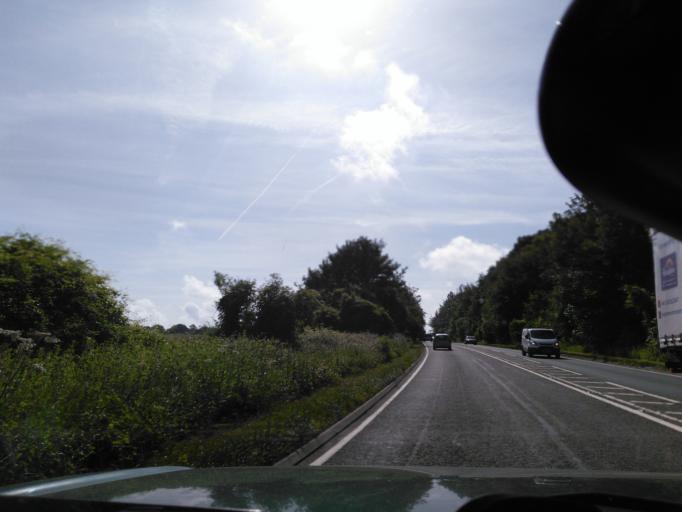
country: GB
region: England
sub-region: Wiltshire
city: Alderbury
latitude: 51.0232
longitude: -1.7059
